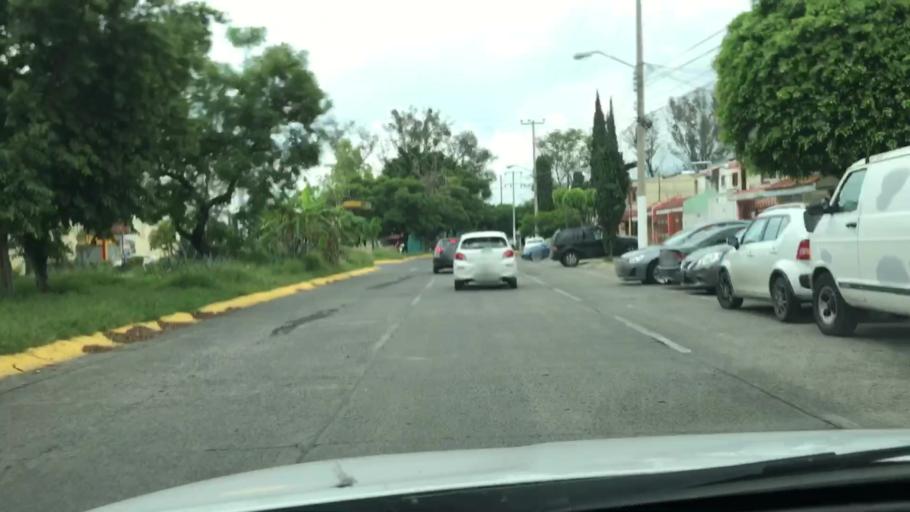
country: MX
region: Jalisco
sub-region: Tlajomulco de Zuniga
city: Palomar
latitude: 20.6330
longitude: -103.4327
